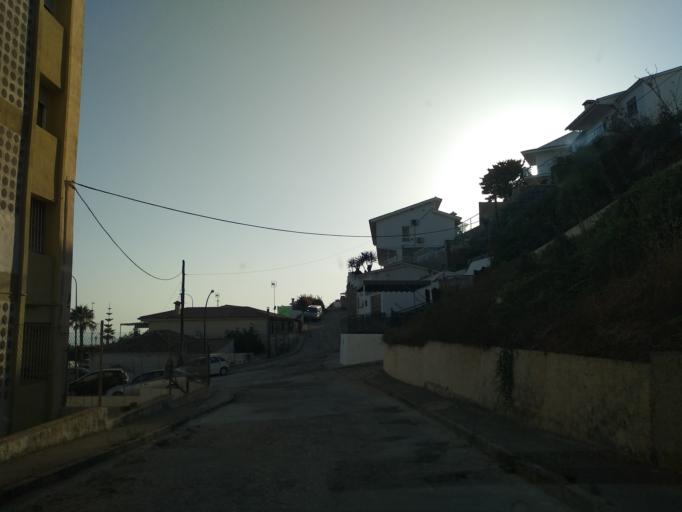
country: ES
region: Andalusia
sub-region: Provincia de Malaga
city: Valdes
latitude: 36.7165
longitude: -4.1911
